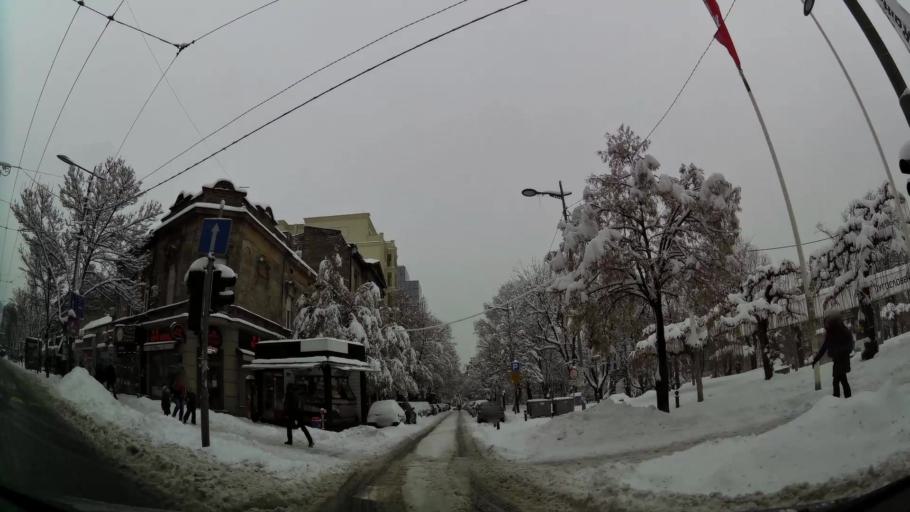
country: RS
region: Central Serbia
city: Belgrade
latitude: 44.8048
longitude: 20.4654
